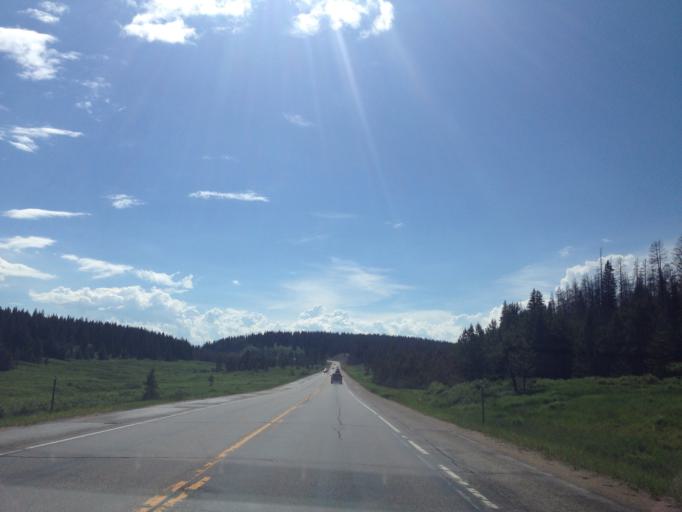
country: US
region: Colorado
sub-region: Routt County
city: Steamboat Springs
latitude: 40.3890
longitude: -106.6622
